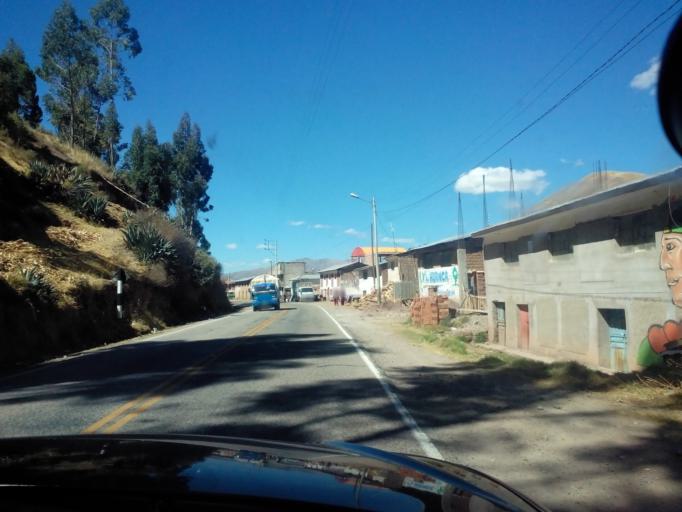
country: PE
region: Cusco
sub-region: Provincia de Canchis
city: Combapata
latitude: -14.0987
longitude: -71.4305
